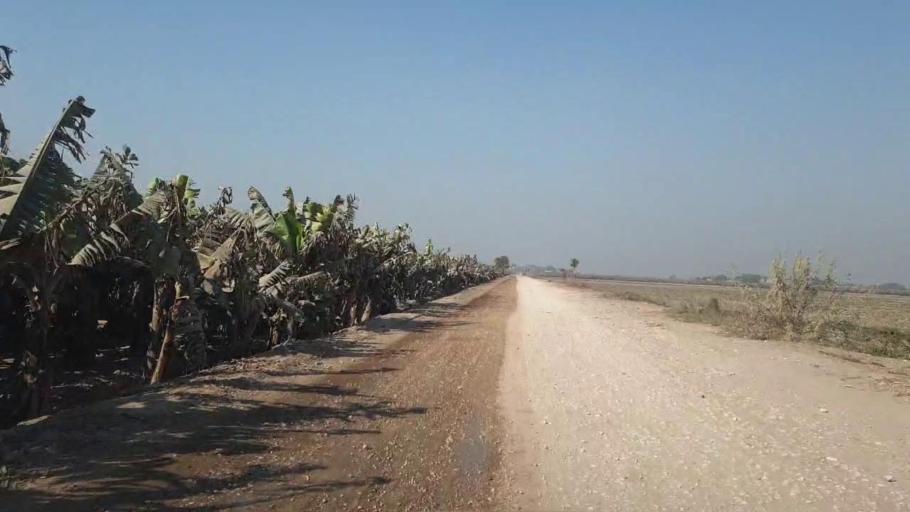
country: PK
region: Sindh
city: Tando Allahyar
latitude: 25.3626
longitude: 68.6592
